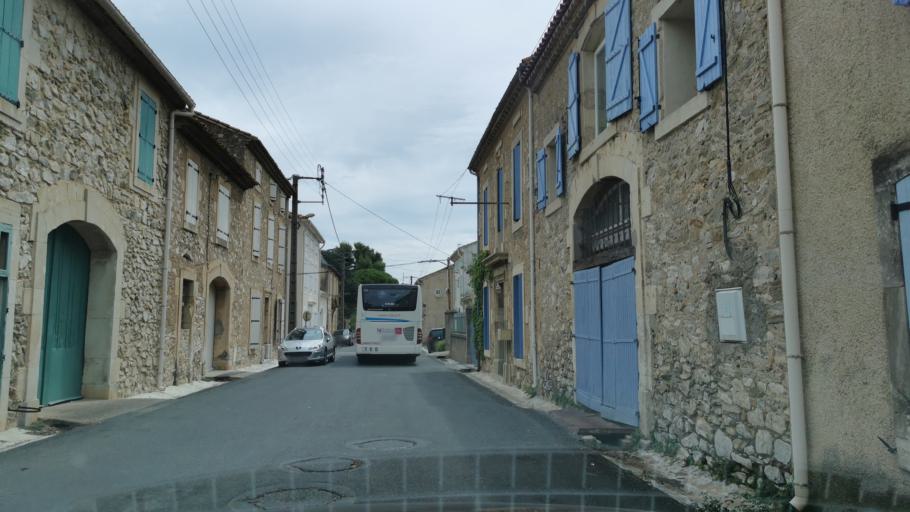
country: FR
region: Languedoc-Roussillon
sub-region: Departement de l'Aude
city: Argeliers
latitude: 43.3101
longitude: 2.9115
